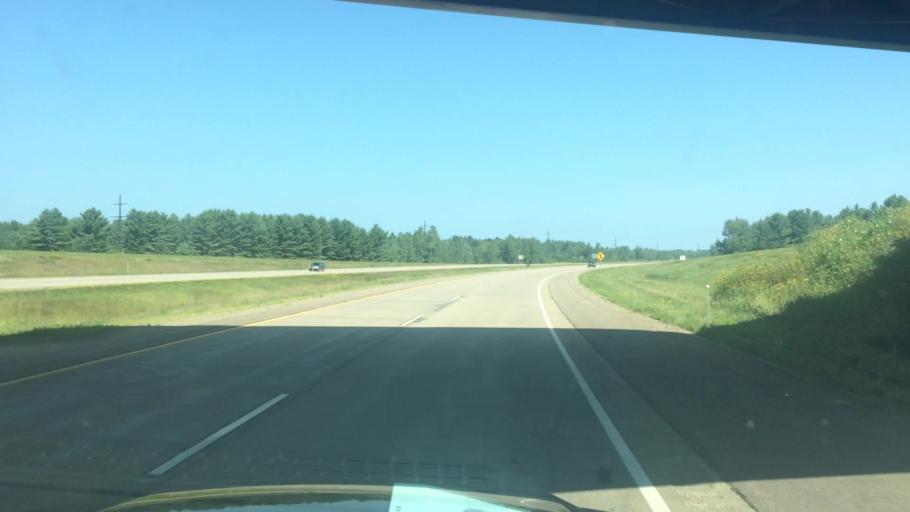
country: US
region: Wisconsin
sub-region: Lincoln County
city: Merrill
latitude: 45.2112
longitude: -89.6676
